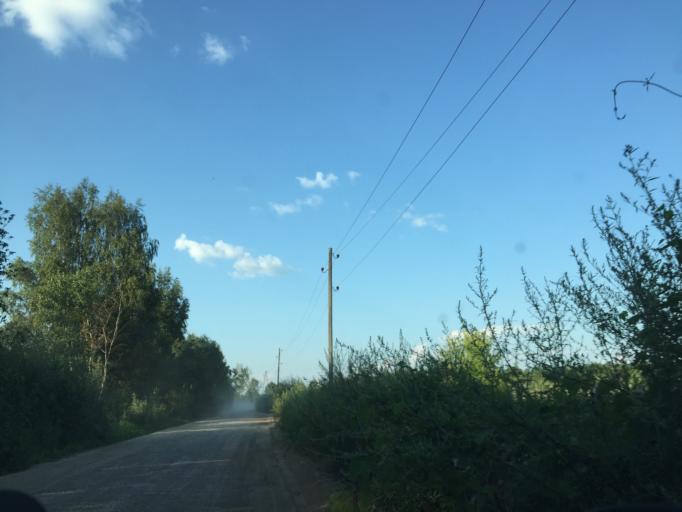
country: LV
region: Riga
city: Bergi
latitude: 56.9738
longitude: 24.3437
